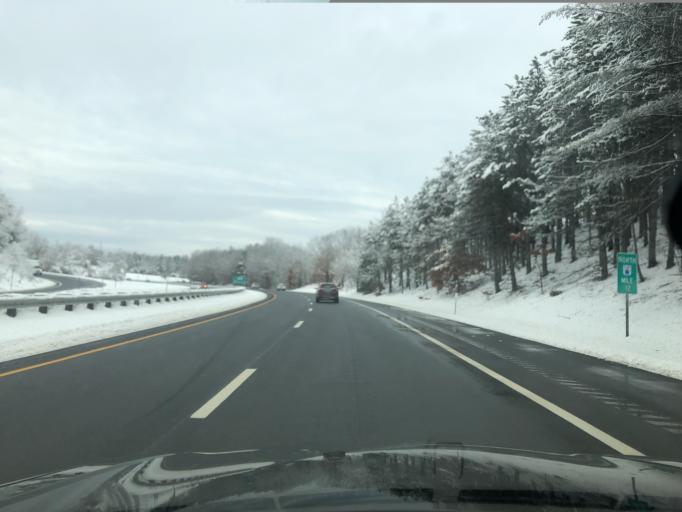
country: US
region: New Hampshire
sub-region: Strafford County
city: Dover
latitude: 43.2143
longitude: -70.8918
